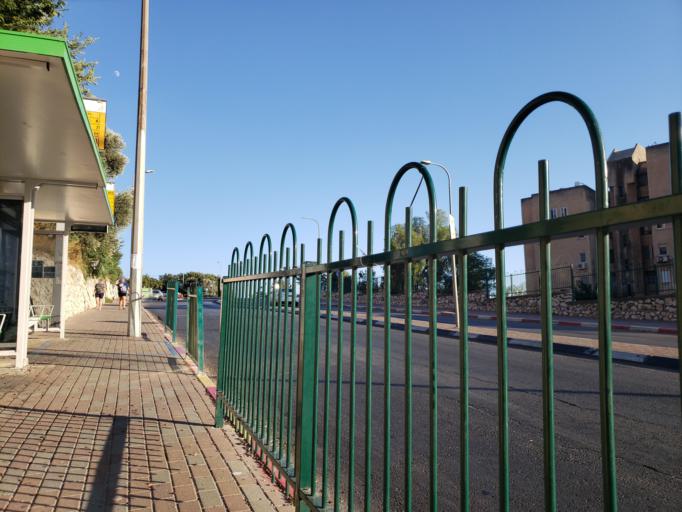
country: IL
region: Northern District
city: Safed
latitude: 32.9588
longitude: 35.4908
